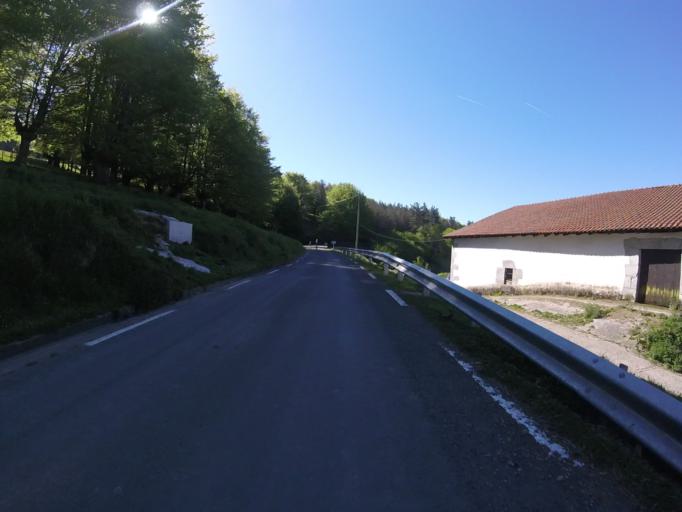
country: ES
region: Basque Country
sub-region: Provincia de Guipuzcoa
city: Errezil
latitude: 43.1982
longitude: -2.2010
